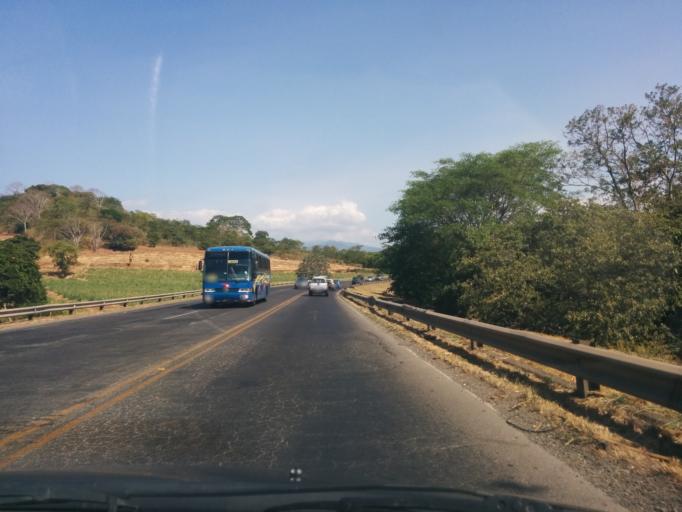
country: CR
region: Alajuela
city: Carrillos
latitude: 10.0052
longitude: -84.3194
